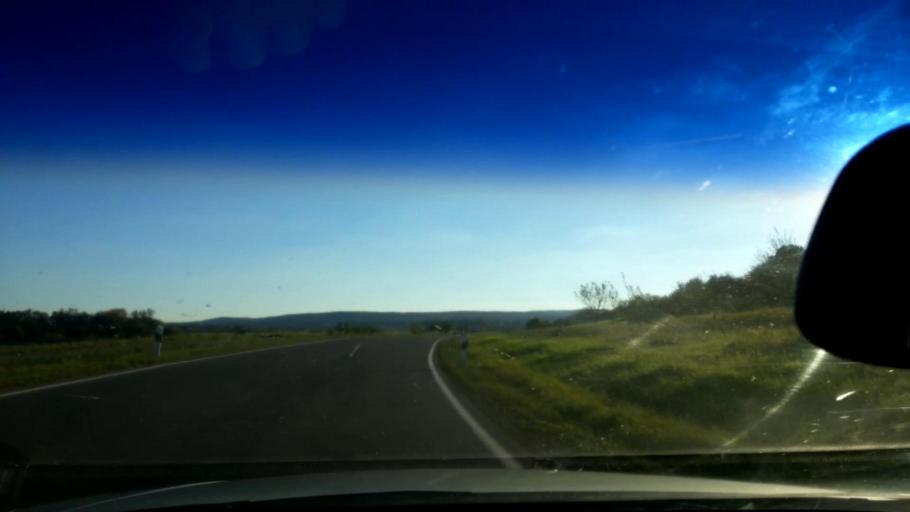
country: DE
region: Bavaria
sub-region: Upper Franconia
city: Rattelsdorf
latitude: 50.0008
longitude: 10.8723
